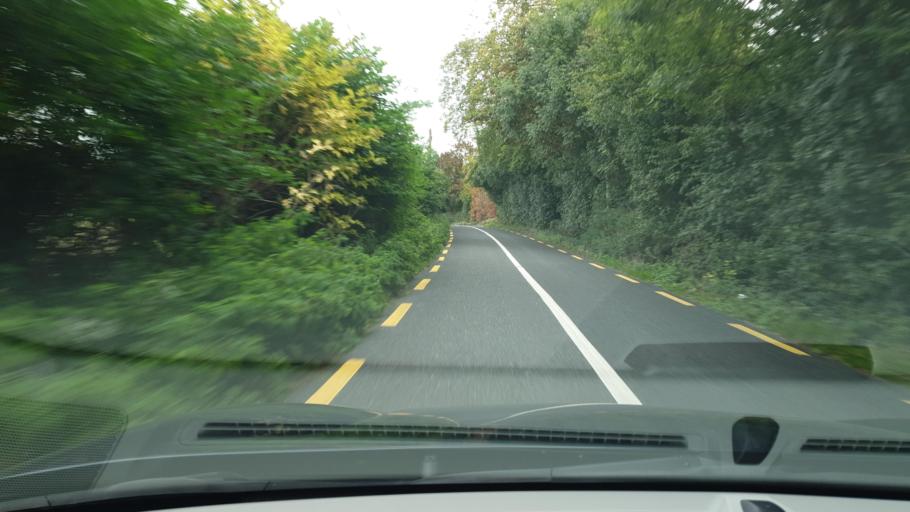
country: IE
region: Leinster
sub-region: Kildare
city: Sallins
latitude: 53.2405
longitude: -6.6835
